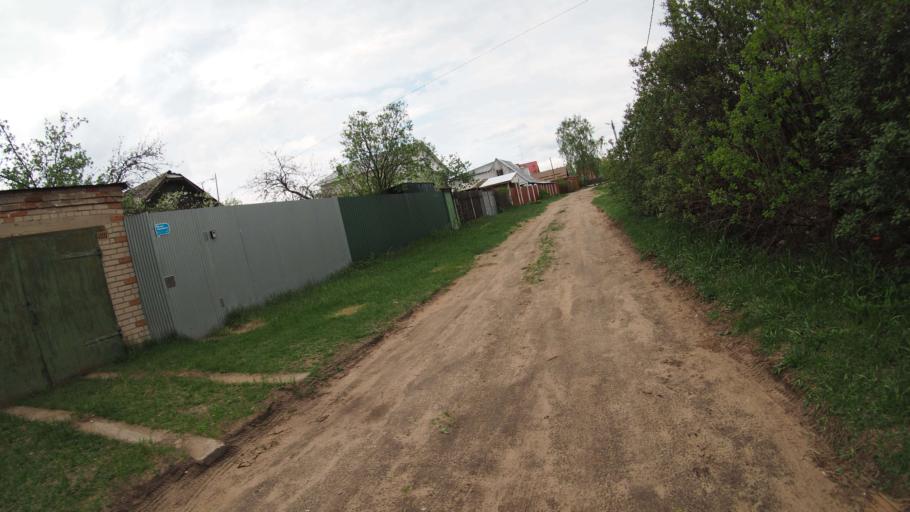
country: RU
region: Moskovskaya
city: Ramenskoye
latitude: 55.5570
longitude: 38.2405
